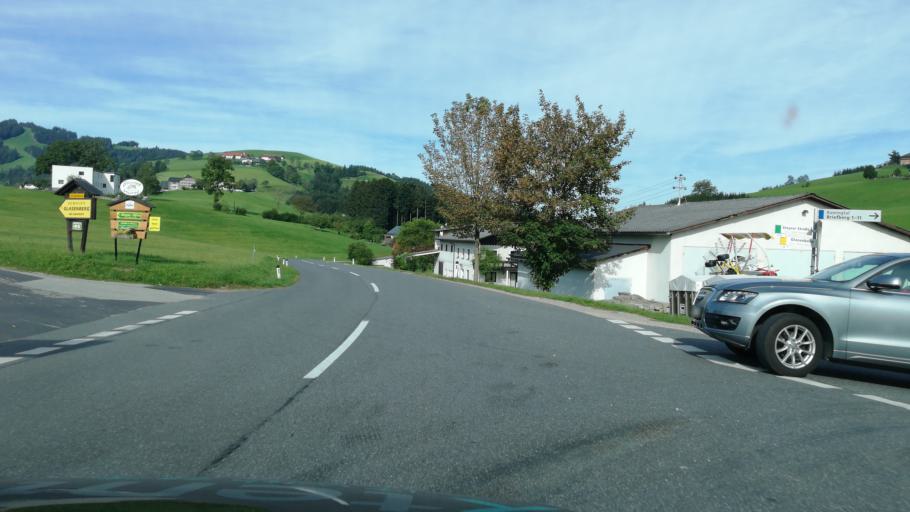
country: AT
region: Upper Austria
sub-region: Politischer Bezirk Steyr-Land
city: Maria Neustift
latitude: 47.9469
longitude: 14.6141
